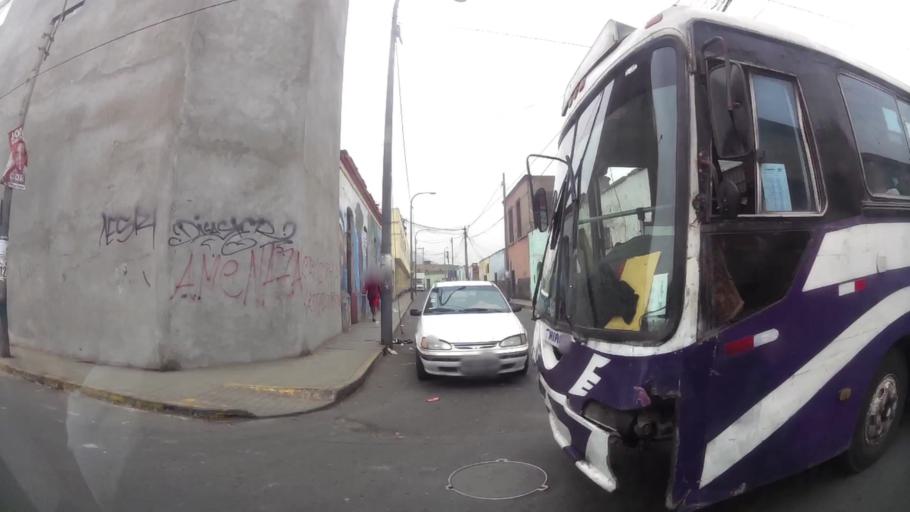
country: PE
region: Lima
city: Lima
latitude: -12.0514
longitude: -77.0167
